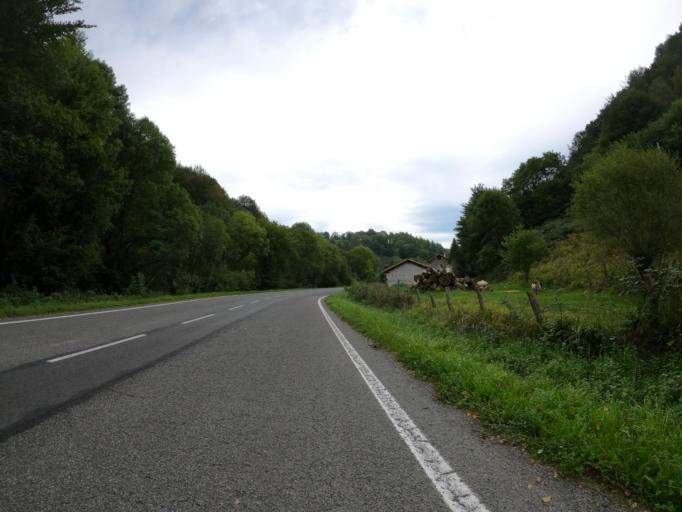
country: ES
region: Navarre
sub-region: Provincia de Navarra
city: Lekunberri
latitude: 43.0289
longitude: -1.9063
